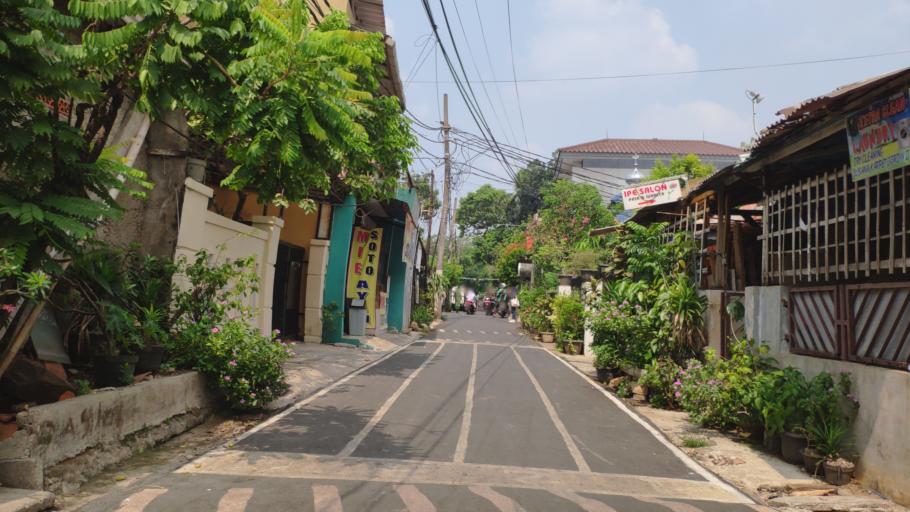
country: ID
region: Banten
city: South Tangerang
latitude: -6.2697
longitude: 106.7730
